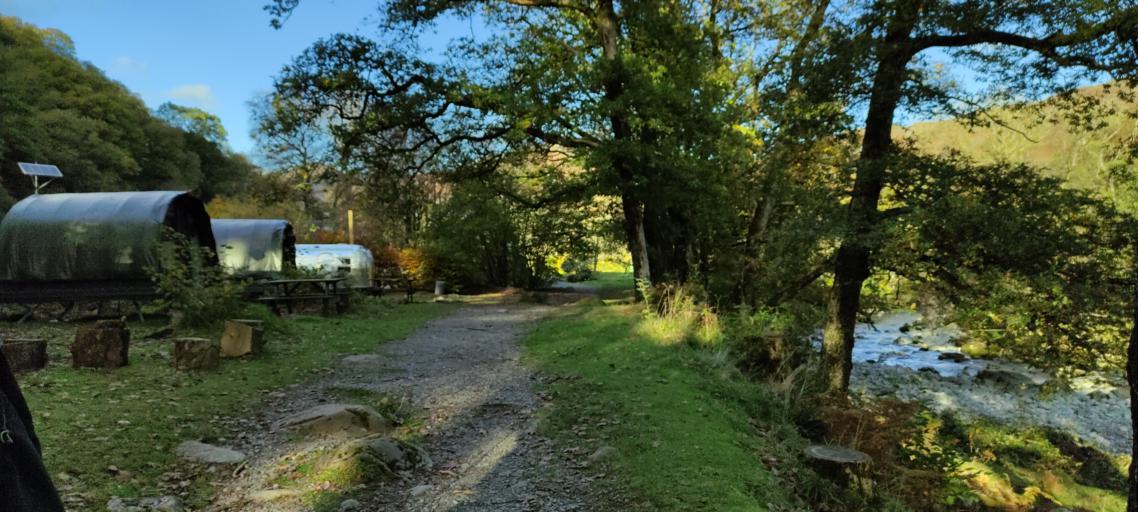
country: GB
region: England
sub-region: Cumbria
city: Keswick
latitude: 54.5171
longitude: -3.1529
